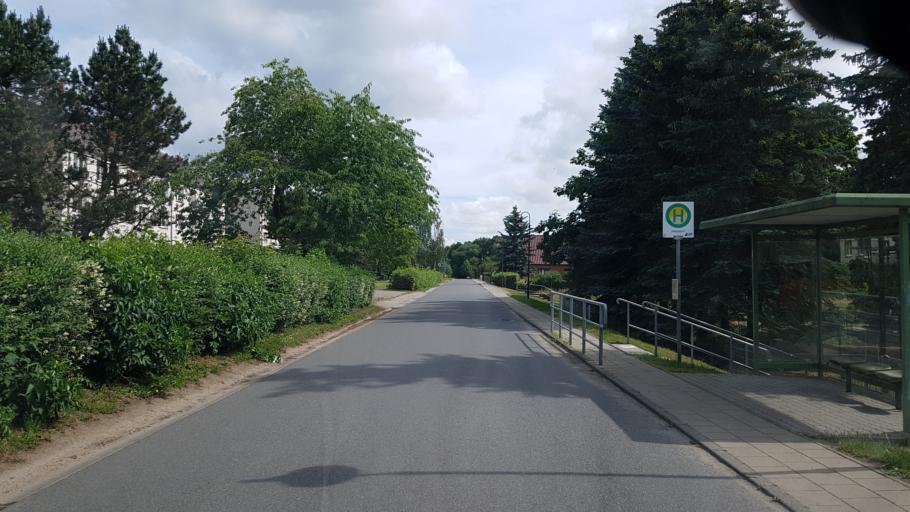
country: DE
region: Mecklenburg-Vorpommern
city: Strasburg
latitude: 53.4344
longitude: 13.7063
